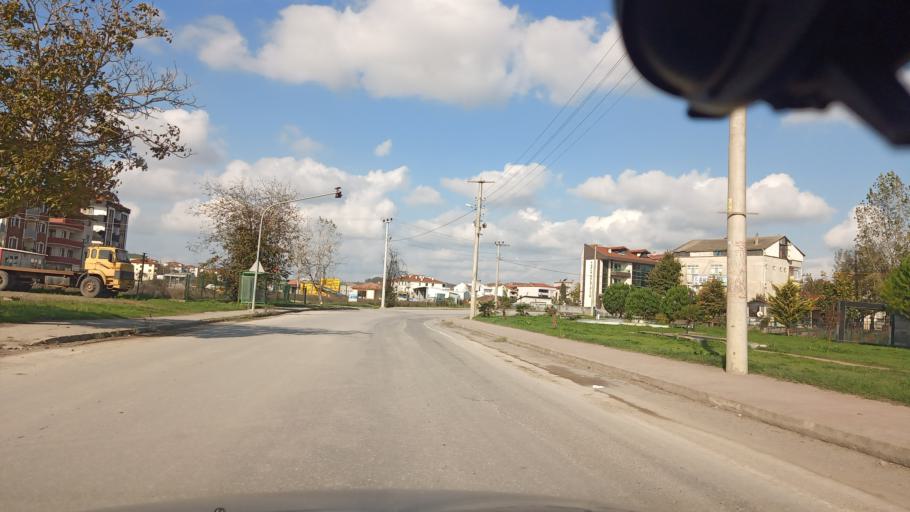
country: TR
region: Sakarya
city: Kaynarca
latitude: 41.0290
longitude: 30.3067
